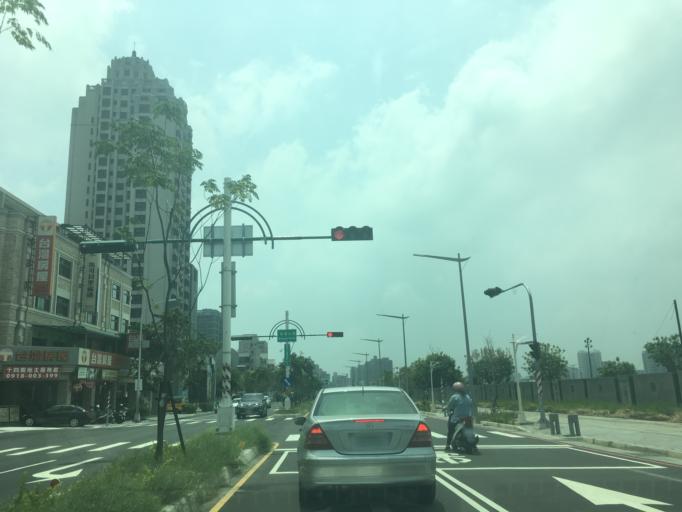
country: TW
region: Taiwan
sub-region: Taichung City
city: Taichung
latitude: 24.1873
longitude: 120.6823
